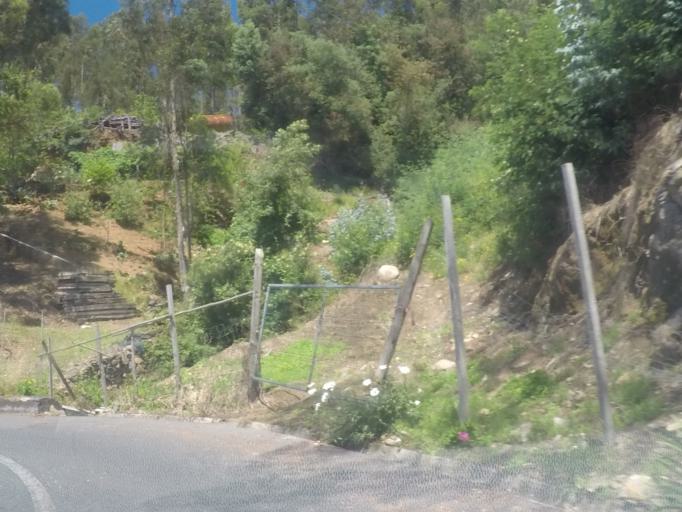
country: PT
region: Madeira
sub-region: Camara de Lobos
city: Curral das Freiras
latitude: 32.6869
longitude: -16.9854
